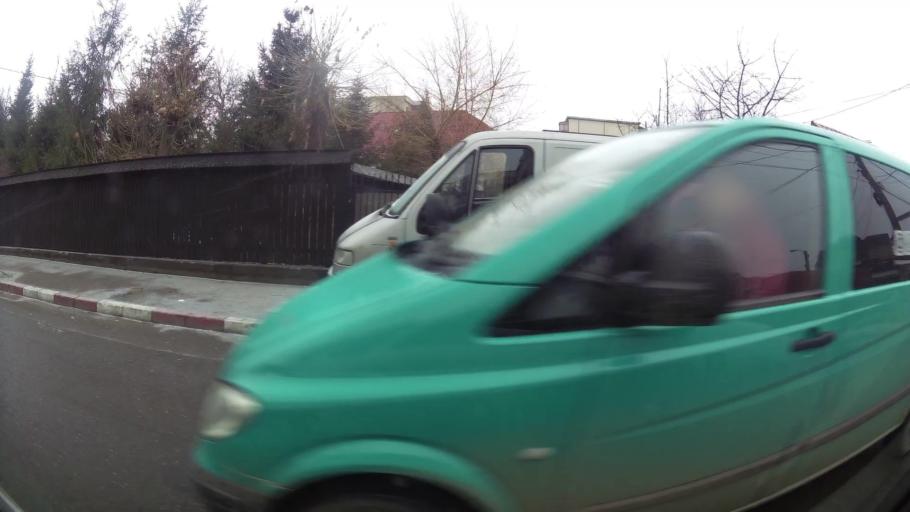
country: RO
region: Prahova
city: Ploiesti
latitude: 44.9405
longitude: 26.0464
